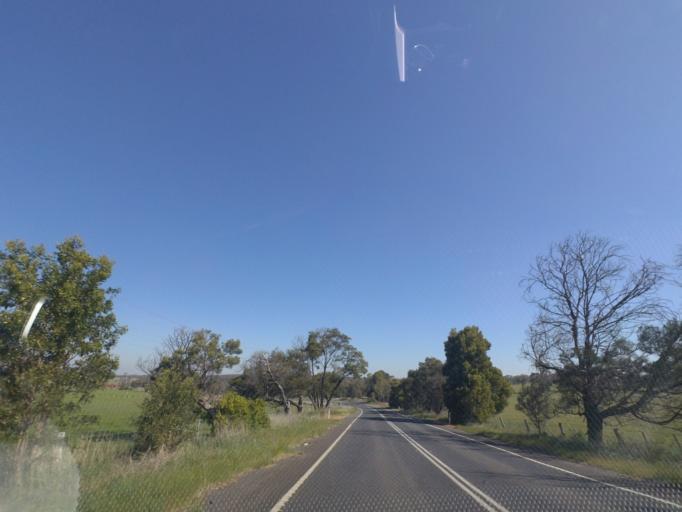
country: AU
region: Victoria
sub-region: Whittlesea
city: Whittlesea
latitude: -37.3351
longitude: 144.9828
